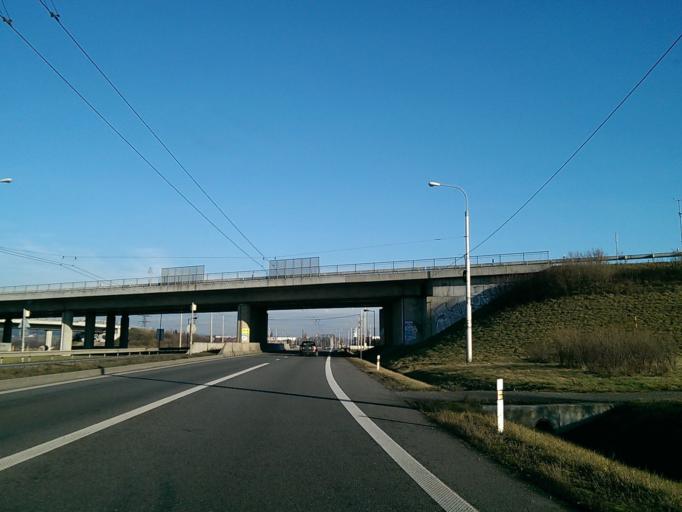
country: CZ
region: Zlin
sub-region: Okres Zlin
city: Otrokovice
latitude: 49.2014
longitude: 17.5516
